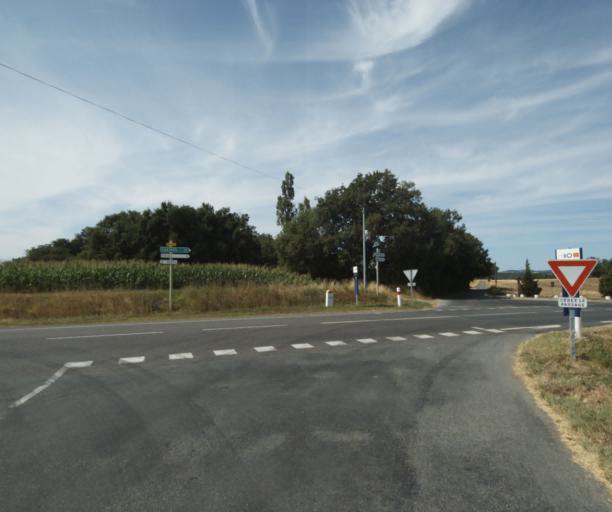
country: FR
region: Midi-Pyrenees
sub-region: Departement du Tarn
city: Soreze
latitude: 43.4996
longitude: 2.0469
